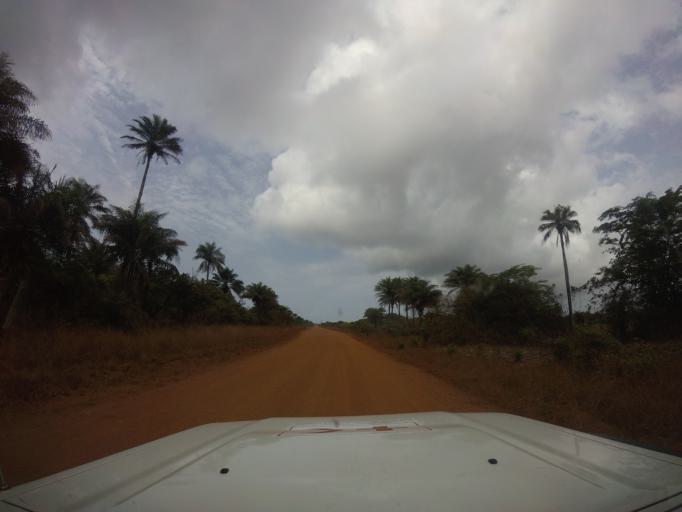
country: LR
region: Grand Cape Mount
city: Robertsport
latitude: 6.7068
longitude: -11.2971
